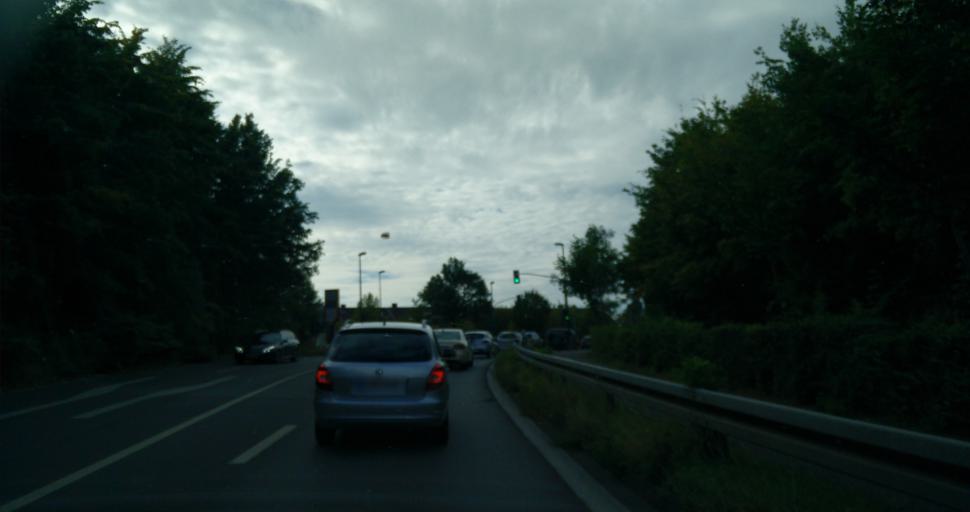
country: DE
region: North Rhine-Westphalia
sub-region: Regierungsbezirk Dusseldorf
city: Meerbusch
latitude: 51.2862
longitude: 6.7401
